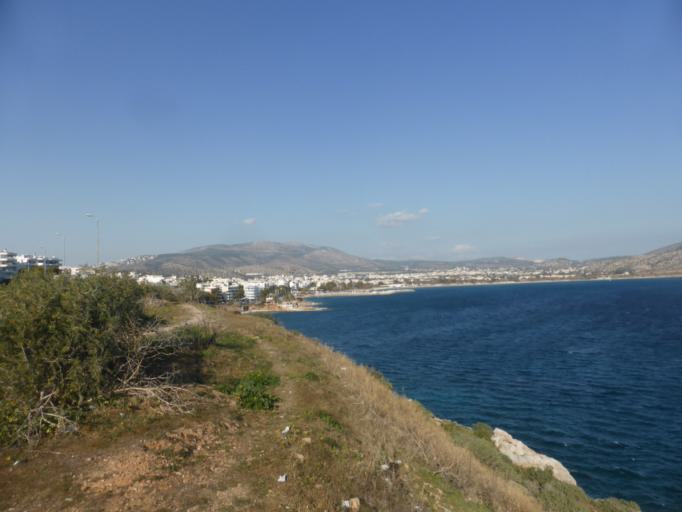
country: GR
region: Attica
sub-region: Nomarchia Anatolikis Attikis
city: Vouliagmeni
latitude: 37.8087
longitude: 23.8011
